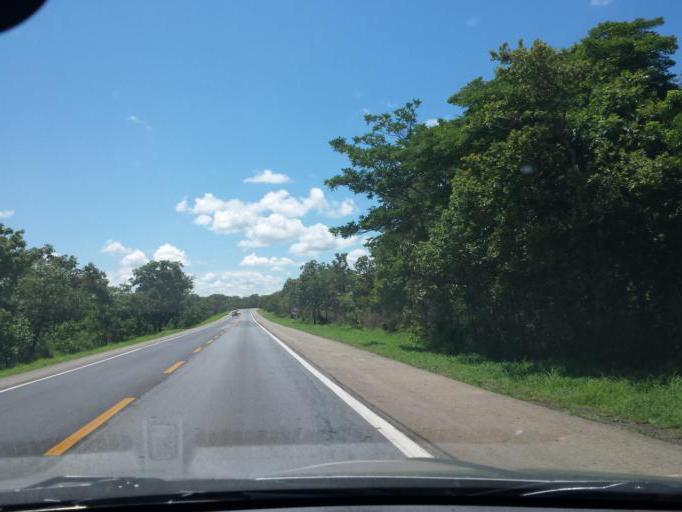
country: BR
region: Goias
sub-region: Luziania
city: Luziania
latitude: -16.4449
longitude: -47.8112
